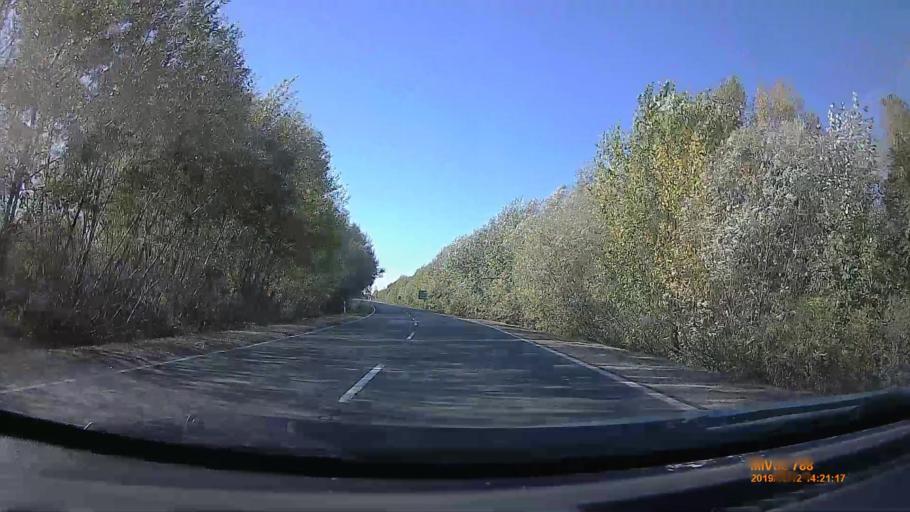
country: HU
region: Hajdu-Bihar
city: Biharkeresztes
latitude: 47.1384
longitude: 21.7368
